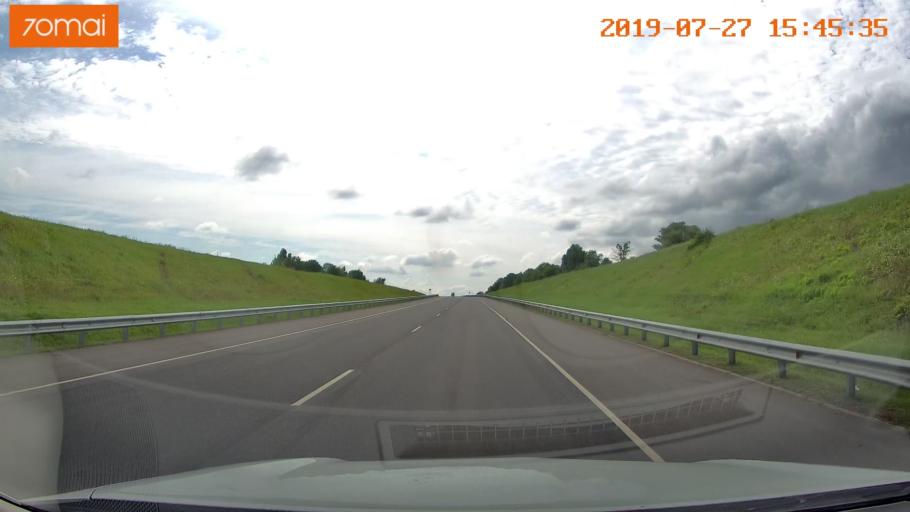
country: RU
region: Kaliningrad
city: Gusev
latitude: 54.6109
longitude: 22.1350
